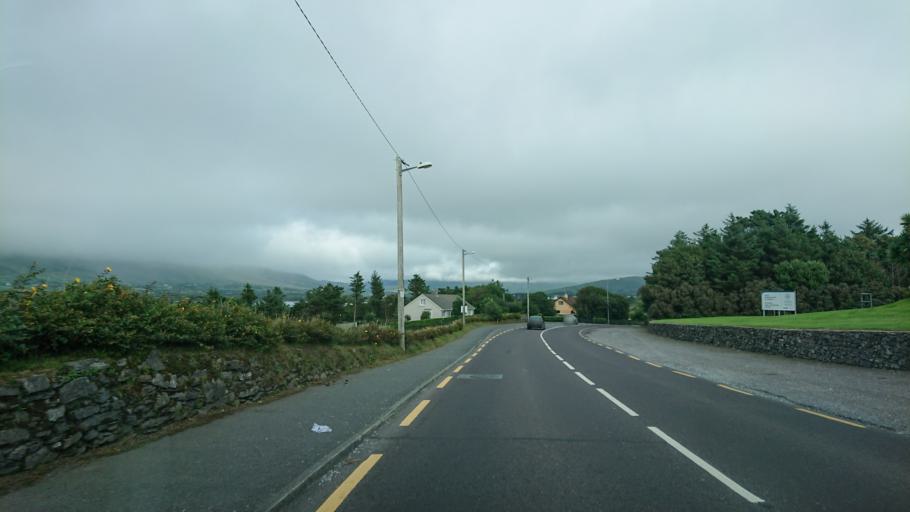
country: IE
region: Munster
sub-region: Ciarrai
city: Cahersiveen
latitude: 51.9508
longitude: -10.2129
